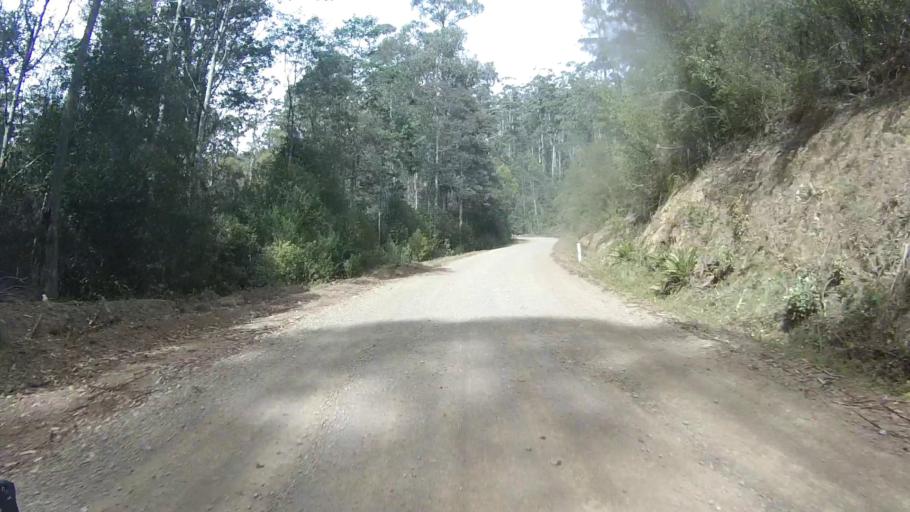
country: AU
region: Tasmania
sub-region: Sorell
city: Sorell
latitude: -42.6956
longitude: 147.8589
